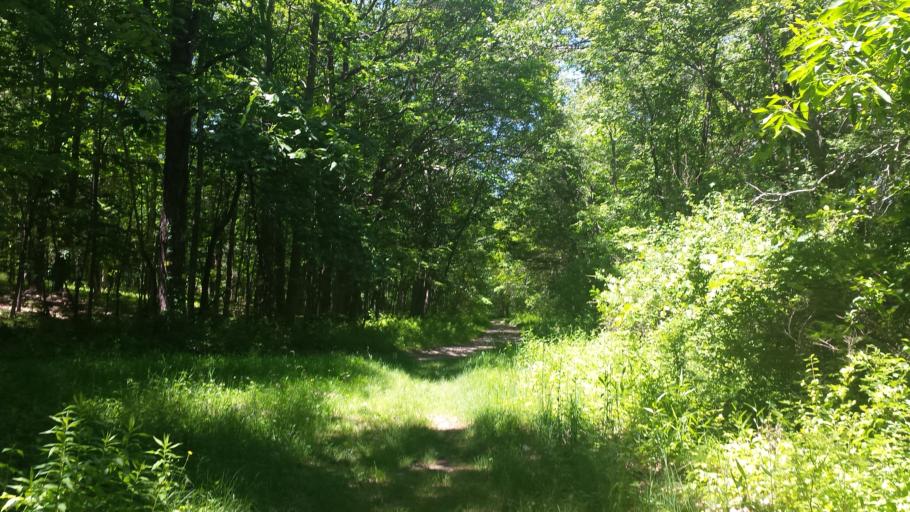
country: US
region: New York
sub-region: Westchester County
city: Pound Ridge
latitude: 41.2473
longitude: -73.5916
